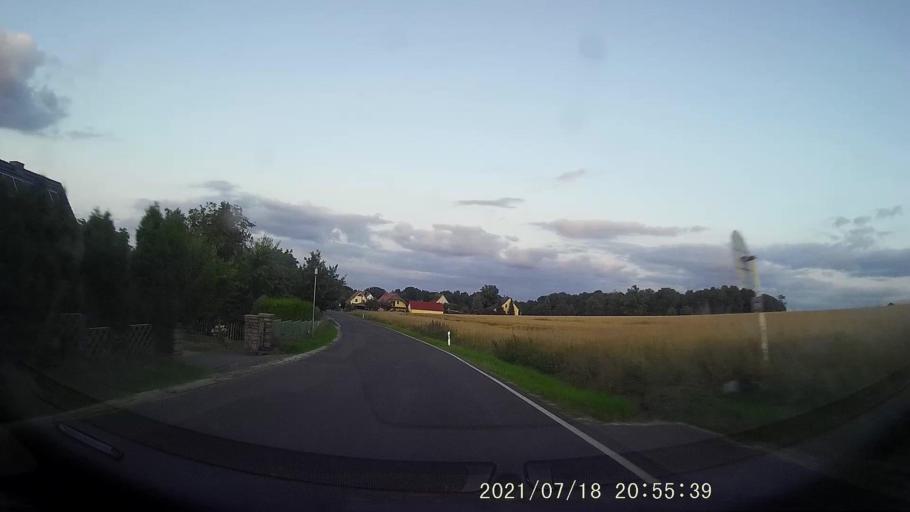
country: DE
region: Saxony
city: Konigshain
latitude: 51.1802
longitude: 14.8777
